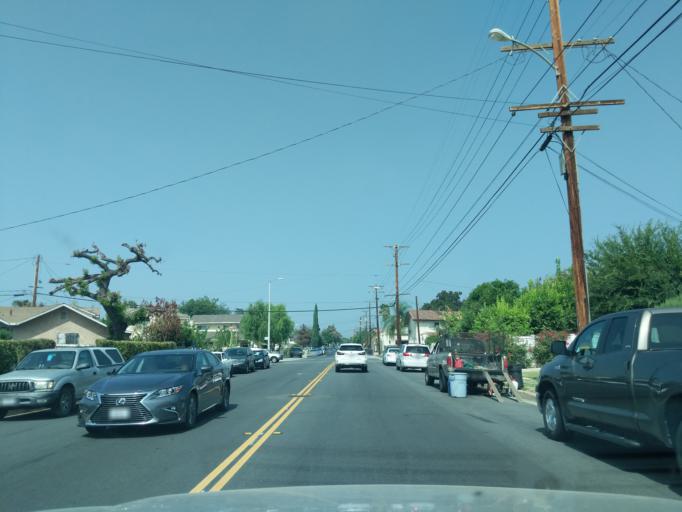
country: US
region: California
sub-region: Los Angeles County
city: East San Gabriel
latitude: 34.0923
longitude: -118.0944
